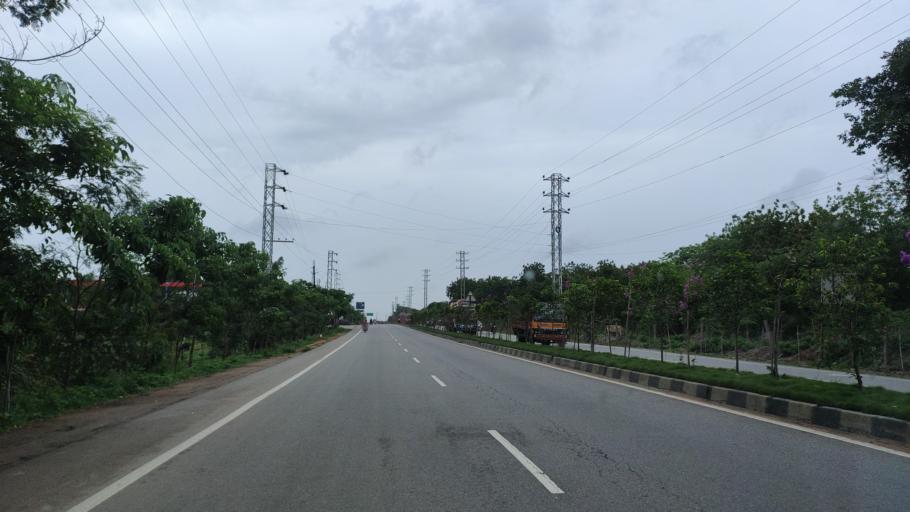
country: IN
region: Telangana
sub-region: Rangareddi
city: Secunderabad
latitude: 17.5875
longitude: 78.5724
